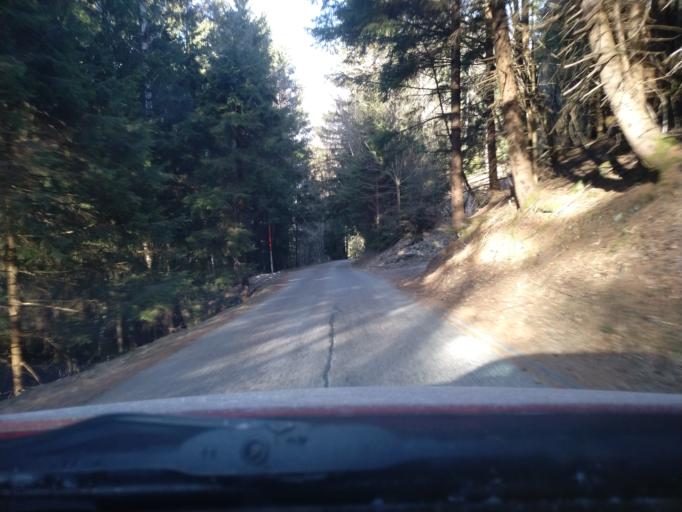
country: AT
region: Carinthia
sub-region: Politischer Bezirk Villach Land
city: Arriach
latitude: 46.7185
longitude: 13.8882
